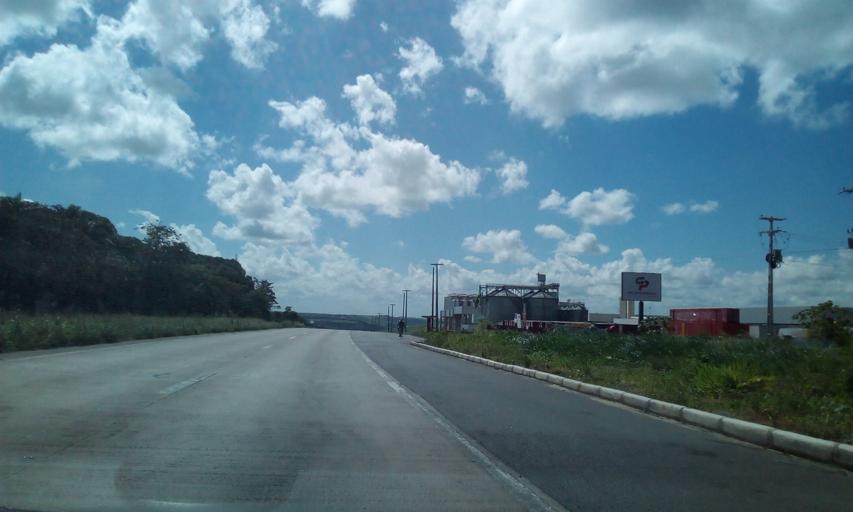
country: BR
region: Pernambuco
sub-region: Itapissuma
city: Itapissuma
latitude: -7.7929
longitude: -34.9284
